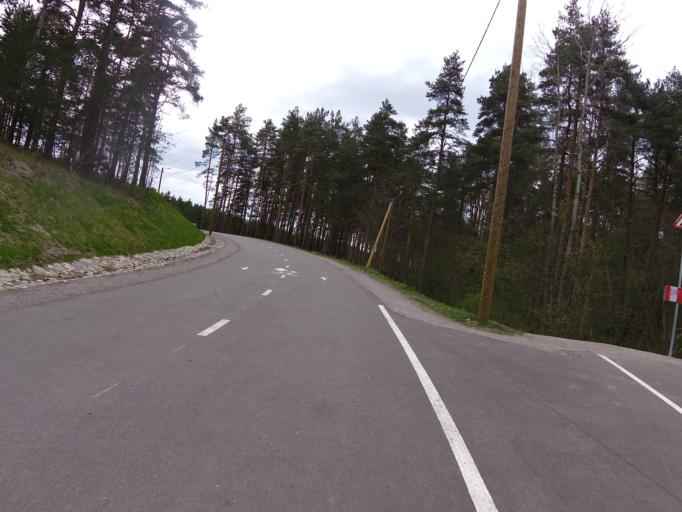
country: EE
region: Harju
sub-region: Tallinna linn
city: Tallinn
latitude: 59.3954
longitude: 24.7315
